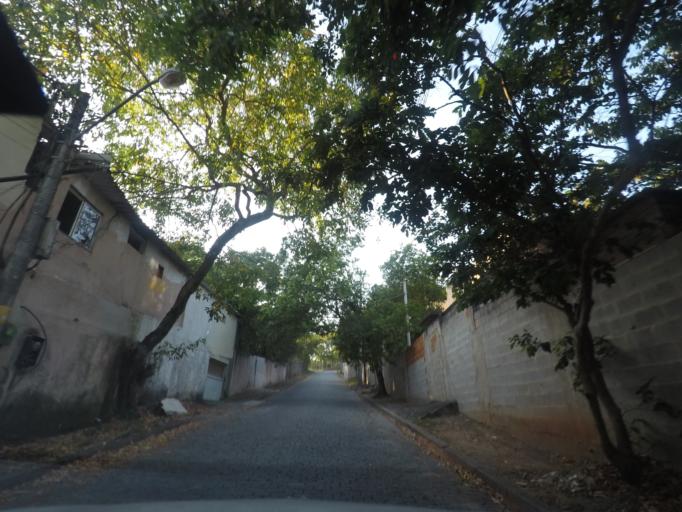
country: BR
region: Rio de Janeiro
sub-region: Rio De Janeiro
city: Rio de Janeiro
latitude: -22.9431
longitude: -43.1898
